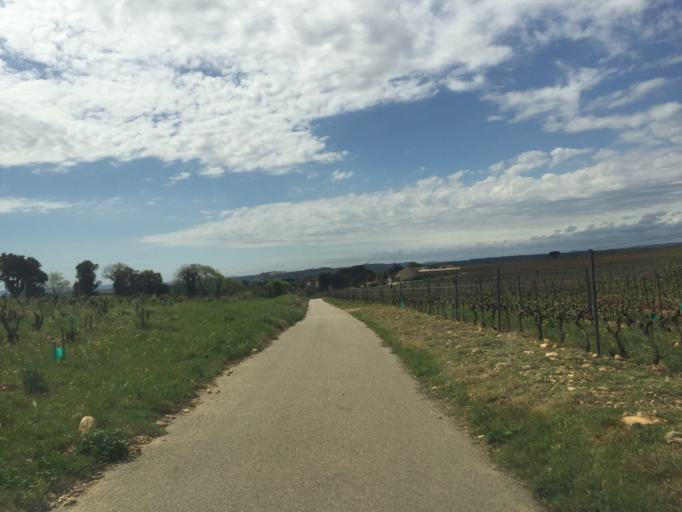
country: FR
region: Provence-Alpes-Cote d'Azur
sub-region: Departement du Vaucluse
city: Chateauneuf-du-Pape
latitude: 44.0585
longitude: 4.8552
